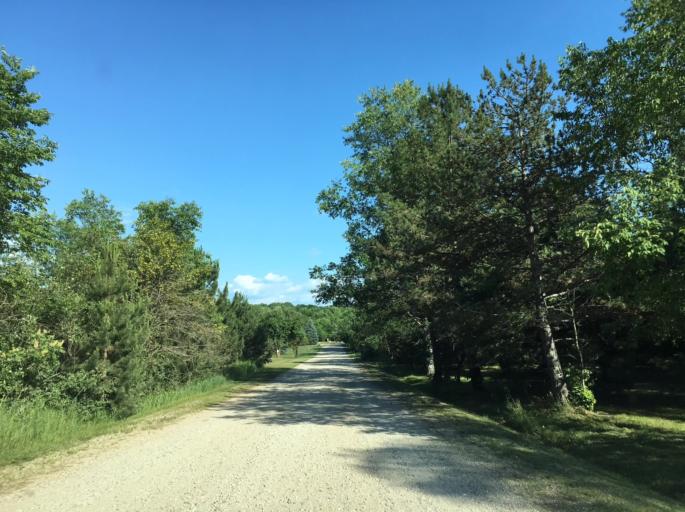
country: US
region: Michigan
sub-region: Osceola County
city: Evart
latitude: 43.8628
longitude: -85.3744
